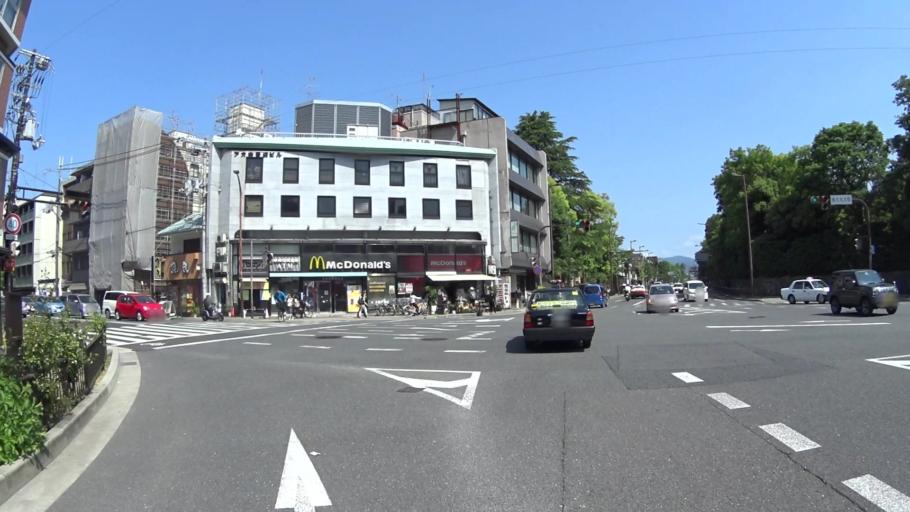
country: JP
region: Kyoto
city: Kyoto
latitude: 35.0172
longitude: 135.7593
